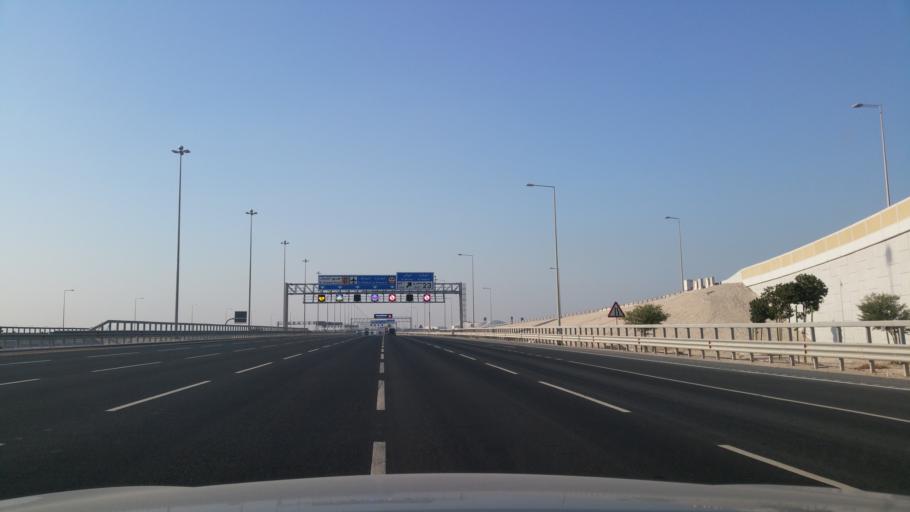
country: QA
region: Al Wakrah
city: Al Wakrah
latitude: 25.1358
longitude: 51.5843
